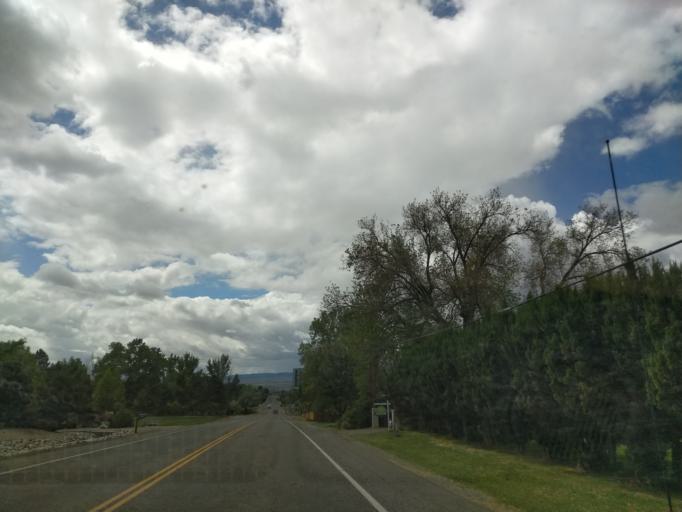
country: US
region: Colorado
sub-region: Mesa County
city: Grand Junction
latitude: 39.1008
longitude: -108.5617
